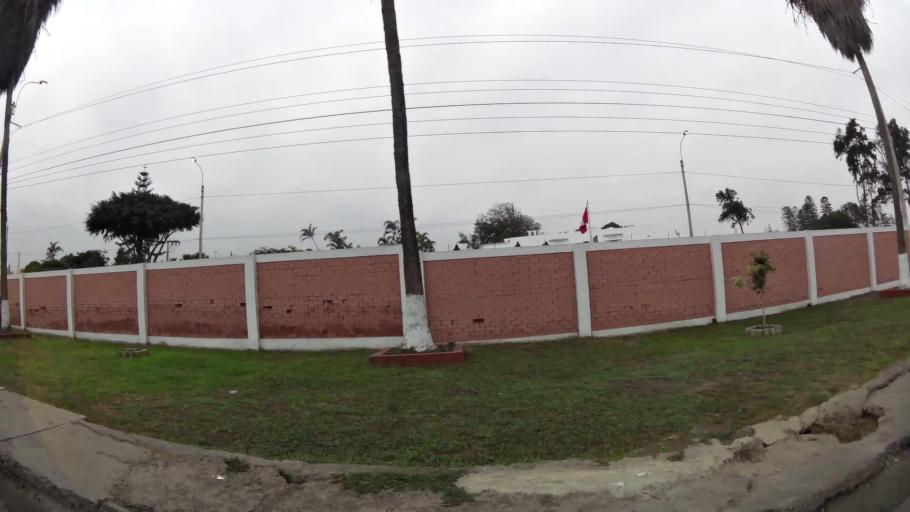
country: PE
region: Lima
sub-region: Lima
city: Surco
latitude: -12.1574
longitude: -77.0192
